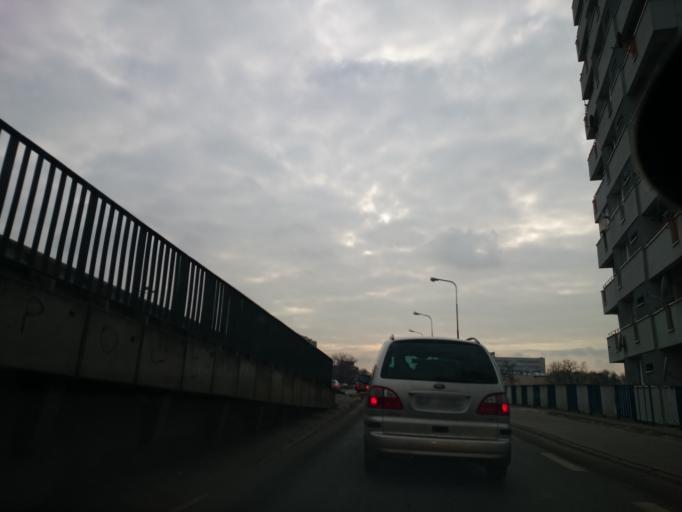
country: PL
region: Opole Voivodeship
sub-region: Powiat opolski
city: Opole
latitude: 50.6736
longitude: 17.9169
